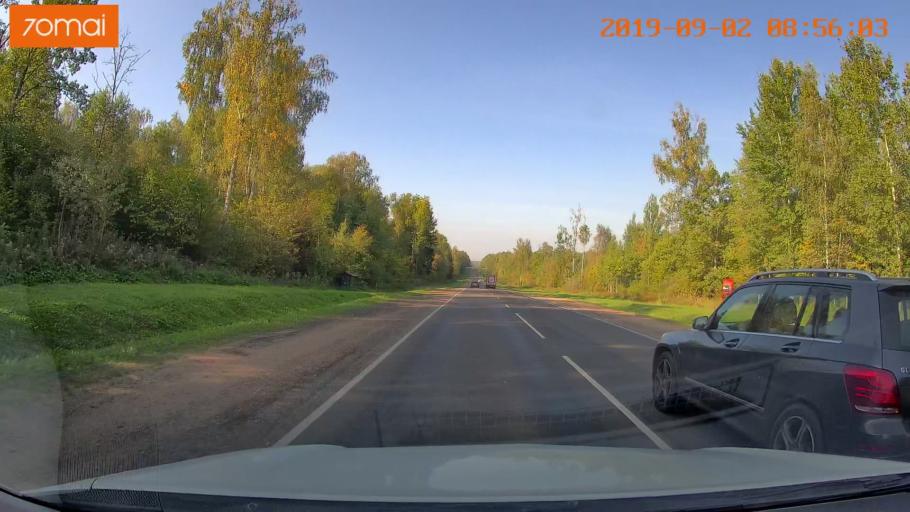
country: RU
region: Kaluga
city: Medyn'
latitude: 54.9487
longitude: 35.8021
